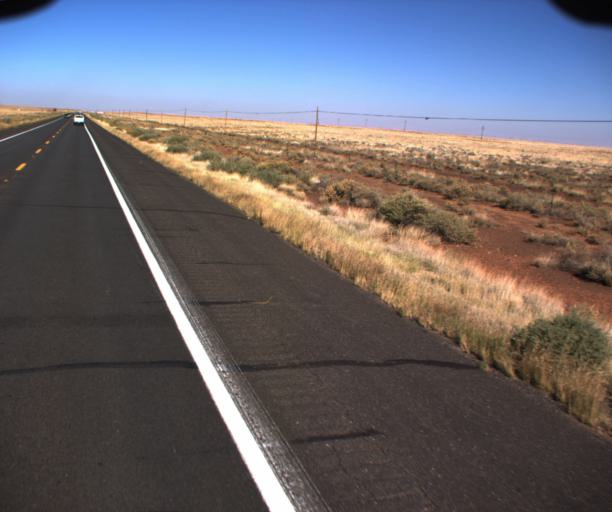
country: US
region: Arizona
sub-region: Coconino County
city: Flagstaff
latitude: 35.6731
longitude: -111.5095
